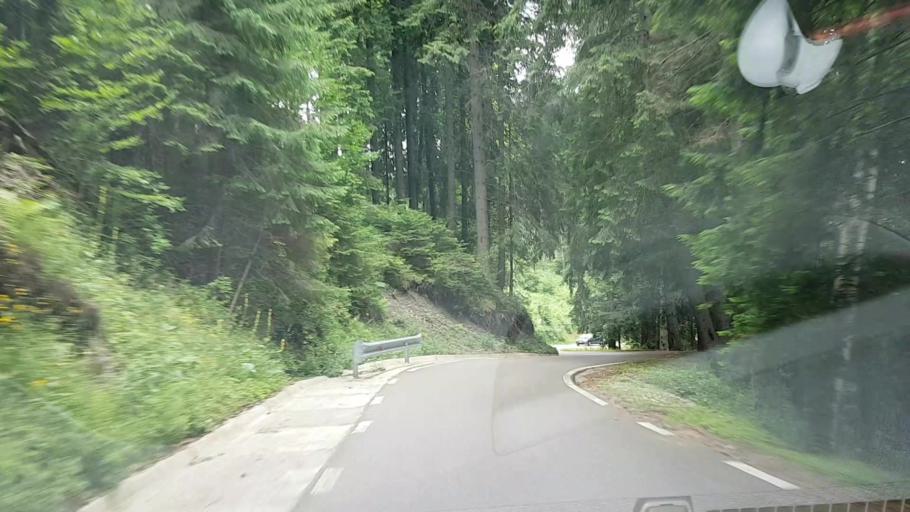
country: RO
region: Suceava
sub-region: Municipiul Campulung Moldovenesc
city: Campulung Moldovenesc
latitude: 47.4363
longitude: 25.5673
